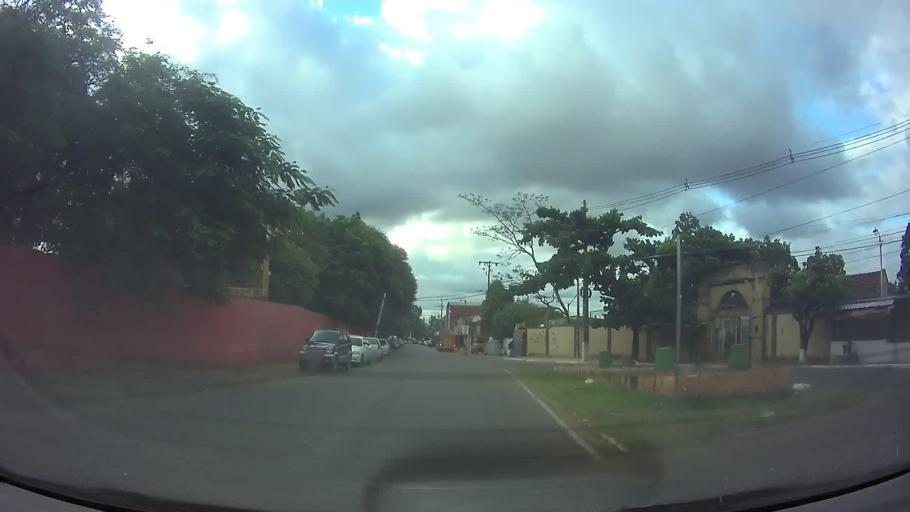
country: PY
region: Central
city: Fernando de la Mora
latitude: -25.3180
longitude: -57.5434
